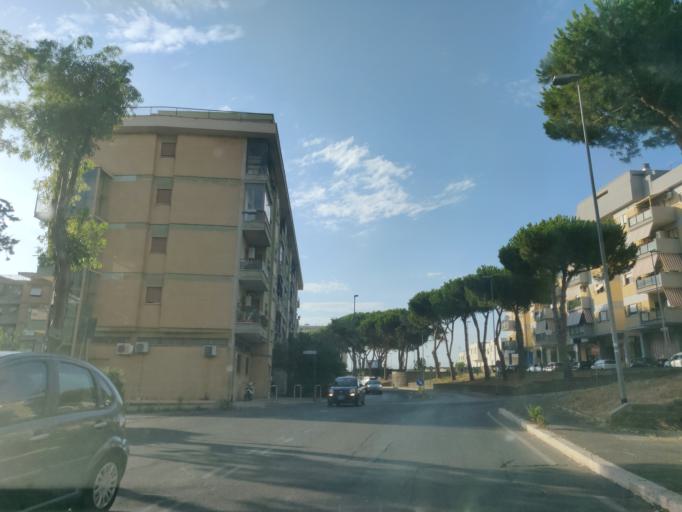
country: IT
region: Latium
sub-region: Citta metropolitana di Roma Capitale
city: Civitavecchia
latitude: 42.0814
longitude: 11.8138
